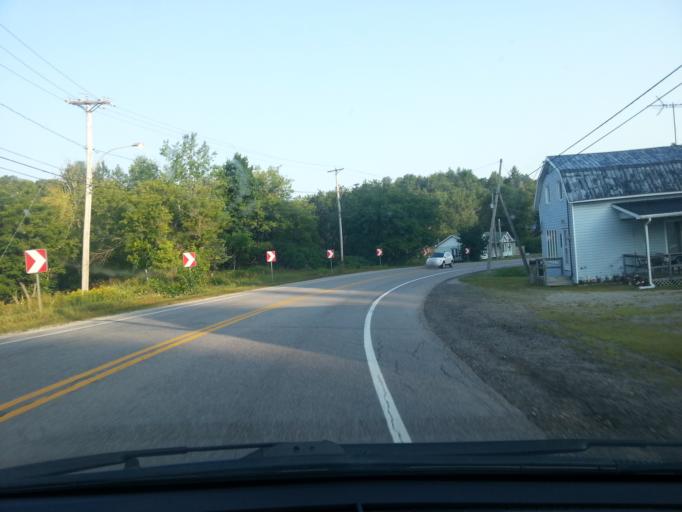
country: CA
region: Quebec
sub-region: Outaouais
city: Wakefield
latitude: 45.7616
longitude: -75.9301
